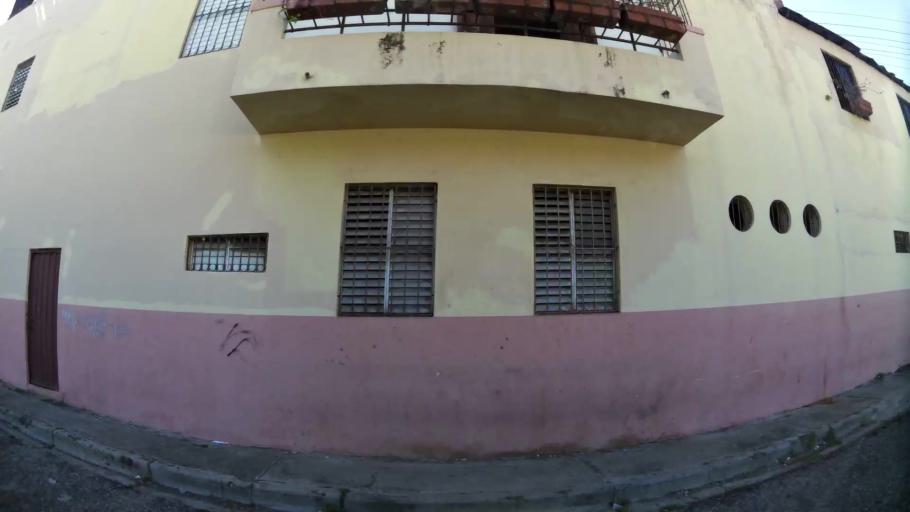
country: DO
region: Nacional
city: Ciudad Nueva
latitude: 18.4690
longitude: -69.8925
